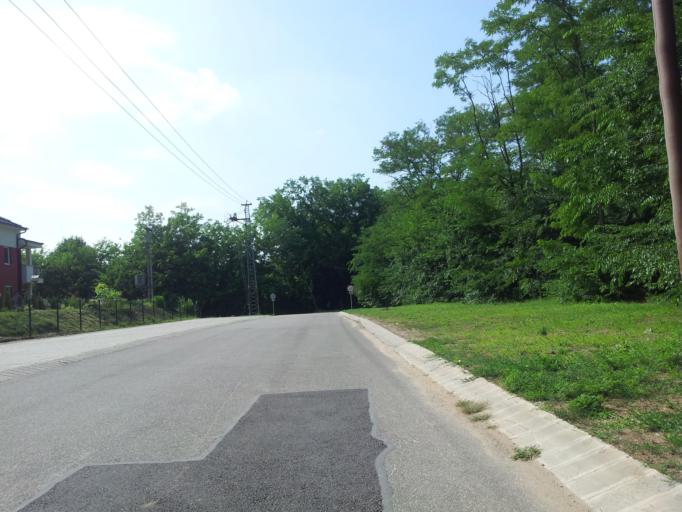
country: HU
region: Pest
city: Orbottyan
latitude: 47.6659
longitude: 19.2679
